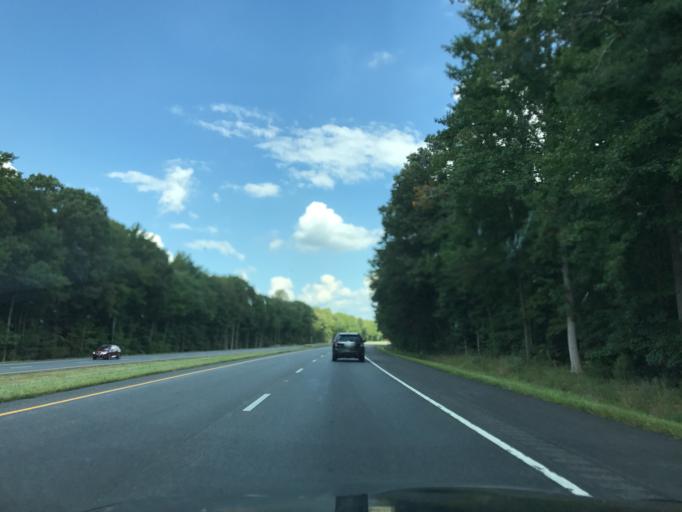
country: US
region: Maryland
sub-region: Queen Anne's County
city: Kingstown
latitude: 39.1881
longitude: -75.9140
